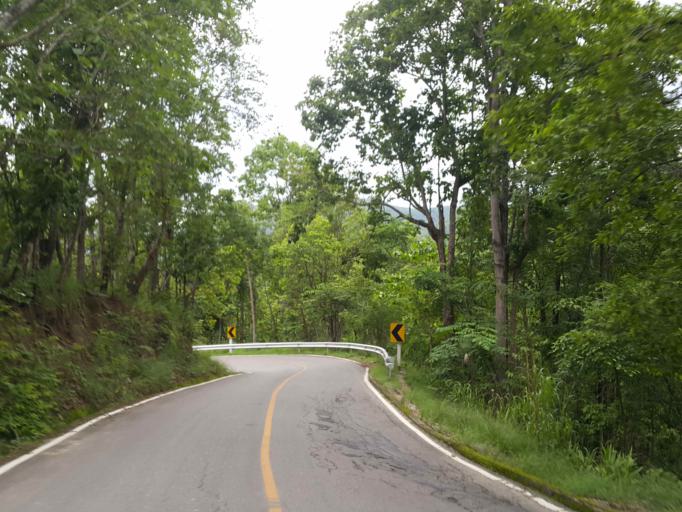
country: TH
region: Chiang Mai
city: Mae Chaem
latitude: 18.5141
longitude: 98.4243
